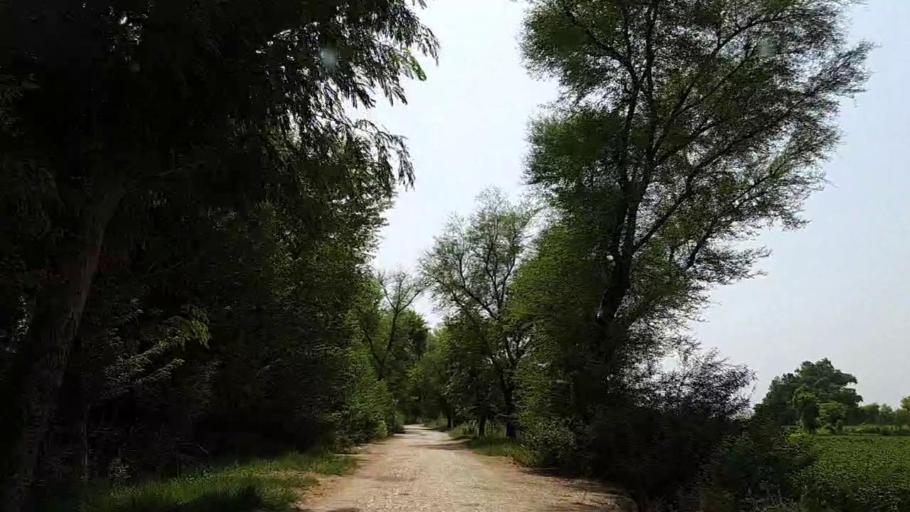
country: PK
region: Sindh
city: Adilpur
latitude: 27.9309
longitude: 69.3839
